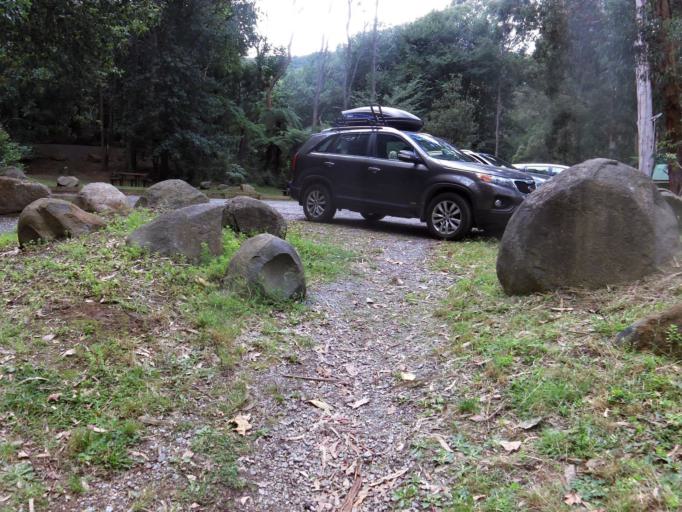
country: AU
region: Victoria
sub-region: Yarra Ranges
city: Olinda
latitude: -37.8475
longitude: 145.3433
